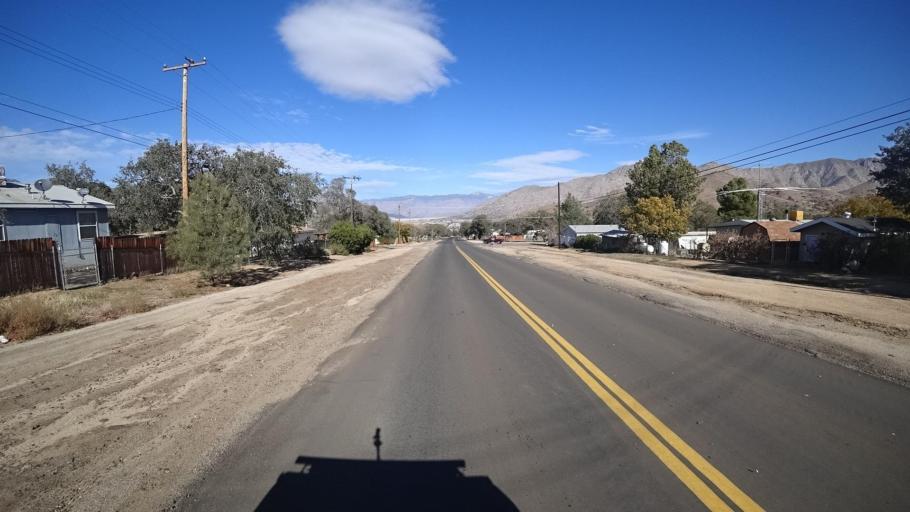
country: US
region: California
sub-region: Kern County
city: Bodfish
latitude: 35.5880
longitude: -118.4966
